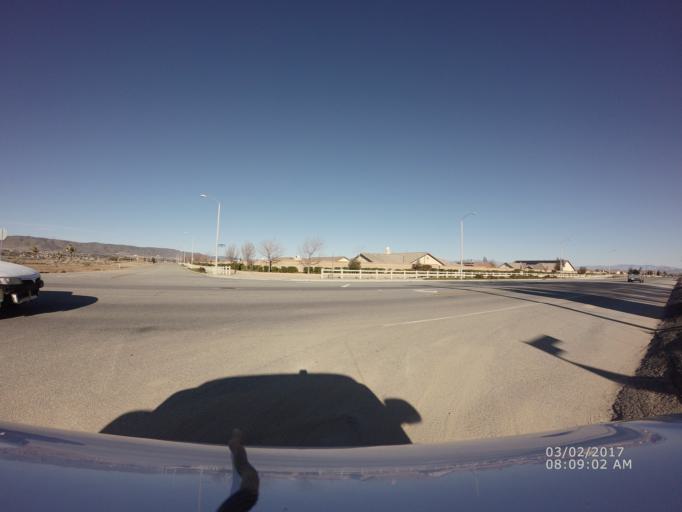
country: US
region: California
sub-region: Los Angeles County
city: Quartz Hill
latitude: 34.6386
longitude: -118.1831
